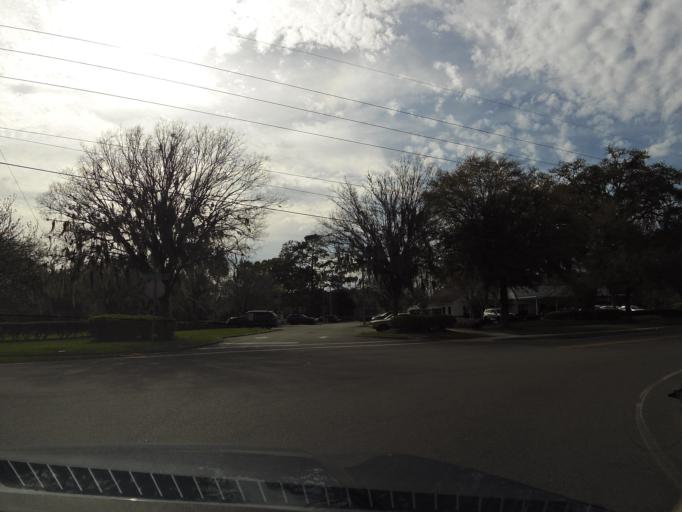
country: US
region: Florida
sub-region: Duval County
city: Jacksonville
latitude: 30.2985
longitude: -81.7668
